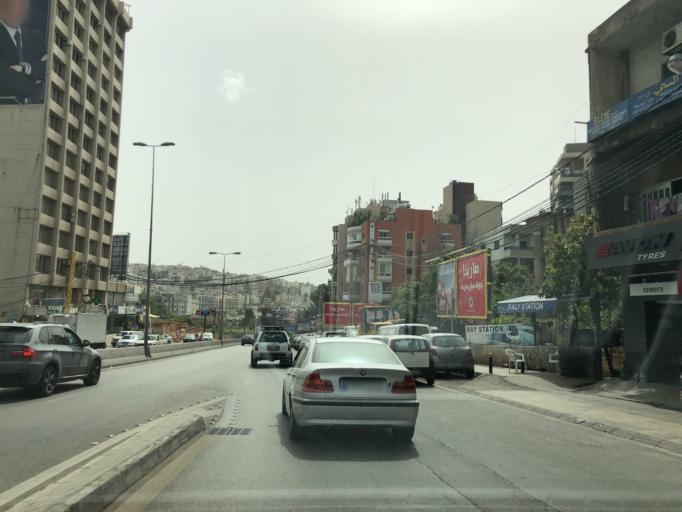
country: LB
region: Mont-Liban
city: Jdaidet el Matn
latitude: 33.8676
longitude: 35.5419
